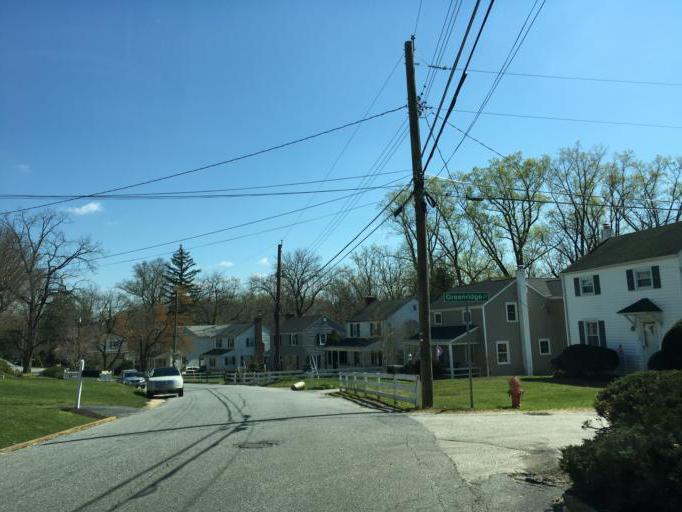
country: US
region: Maryland
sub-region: Baltimore County
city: Lutherville
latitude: 39.4190
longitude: -76.6097
